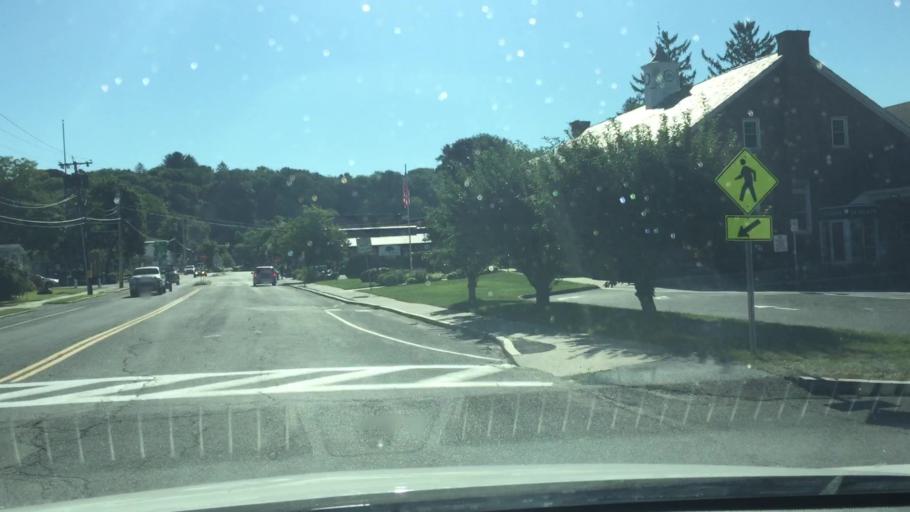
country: US
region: Massachusetts
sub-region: Berkshire County
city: Lee
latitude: 42.3039
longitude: -73.2501
